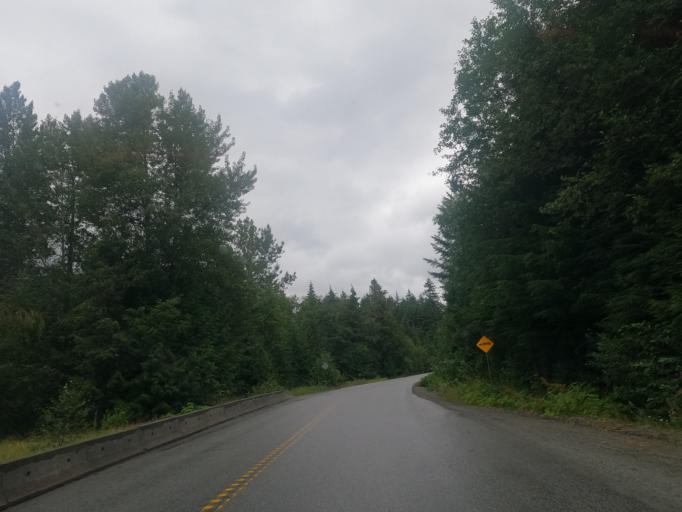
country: CA
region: British Columbia
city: Pemberton
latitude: 50.3127
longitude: -122.5684
